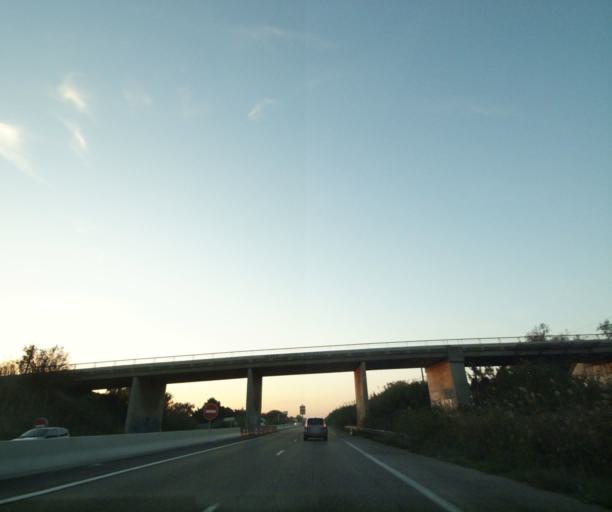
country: FR
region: Provence-Alpes-Cote d'Azur
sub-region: Departement des Bouches-du-Rhone
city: Fontvieille
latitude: 43.6422
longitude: 4.7125
